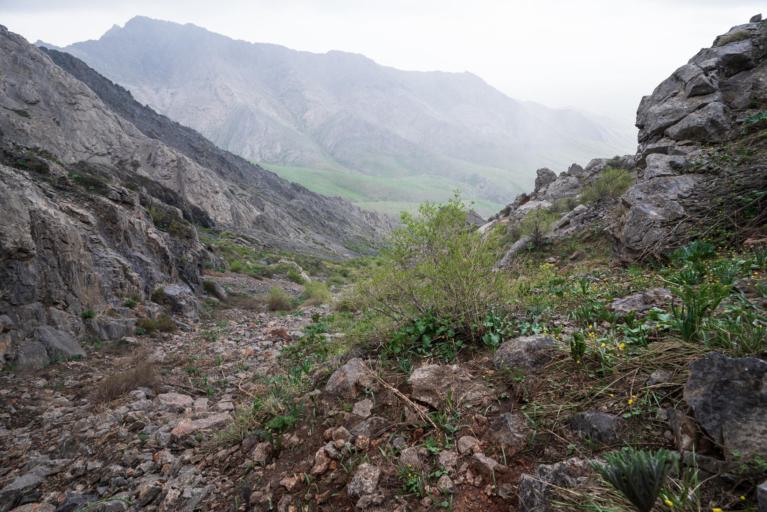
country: KZ
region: Ongtustik Qazaqstan
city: Ashchysay
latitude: 43.6275
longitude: 68.9593
